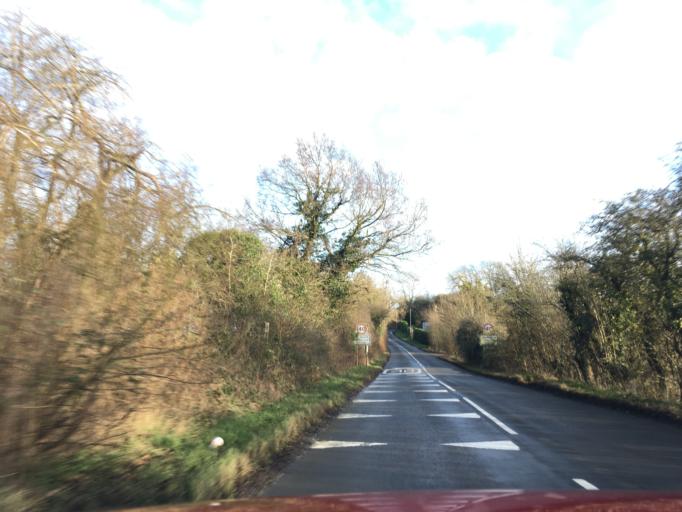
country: GB
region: England
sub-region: Warwickshire
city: Henley in Arden
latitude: 52.2261
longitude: -1.7799
